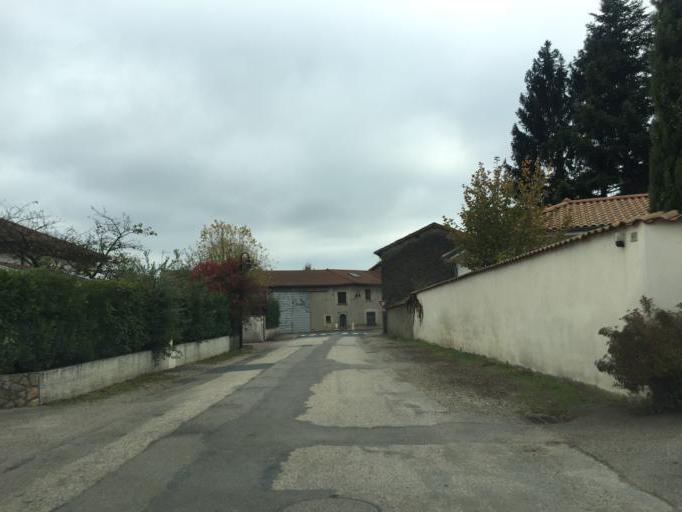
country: FR
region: Rhone-Alpes
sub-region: Departement de l'Ain
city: Tramoyes
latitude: 45.8765
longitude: 4.9652
